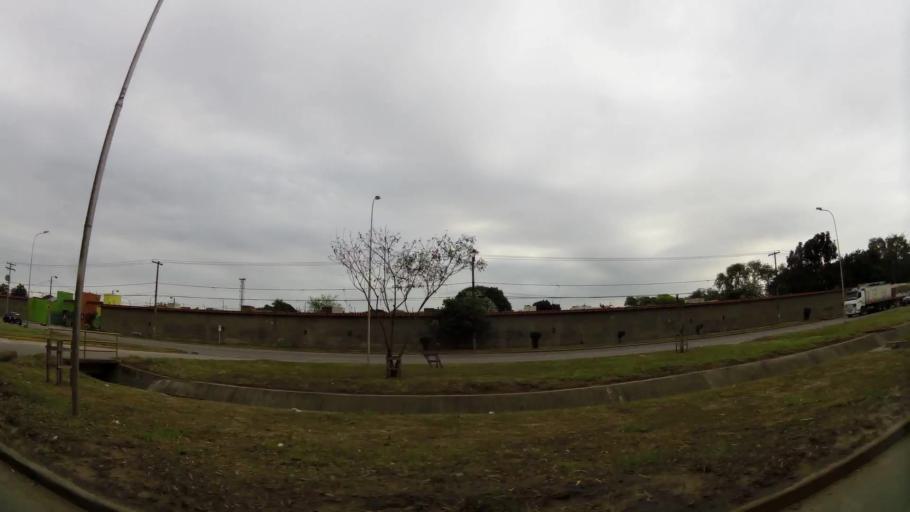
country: BO
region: Santa Cruz
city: Santa Cruz de la Sierra
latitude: -17.8138
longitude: -63.1638
